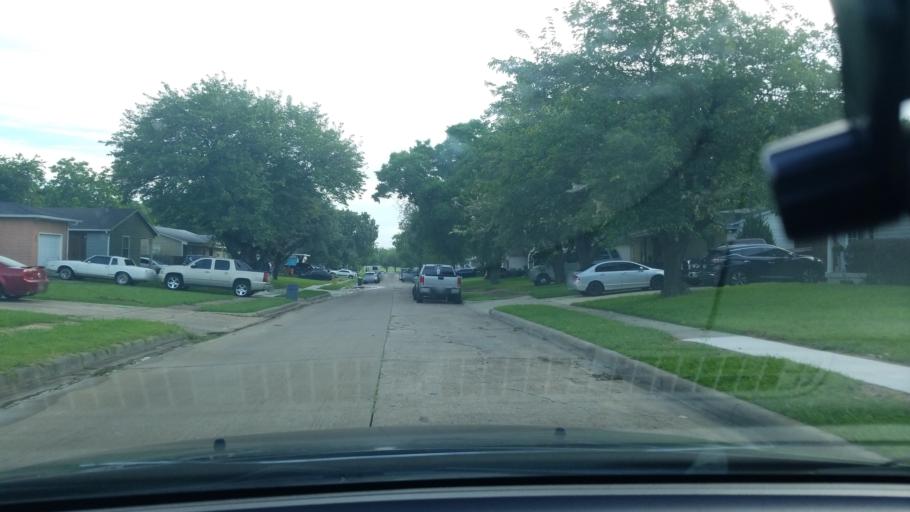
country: US
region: Texas
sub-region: Dallas County
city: Mesquite
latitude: 32.7651
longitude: -96.6373
